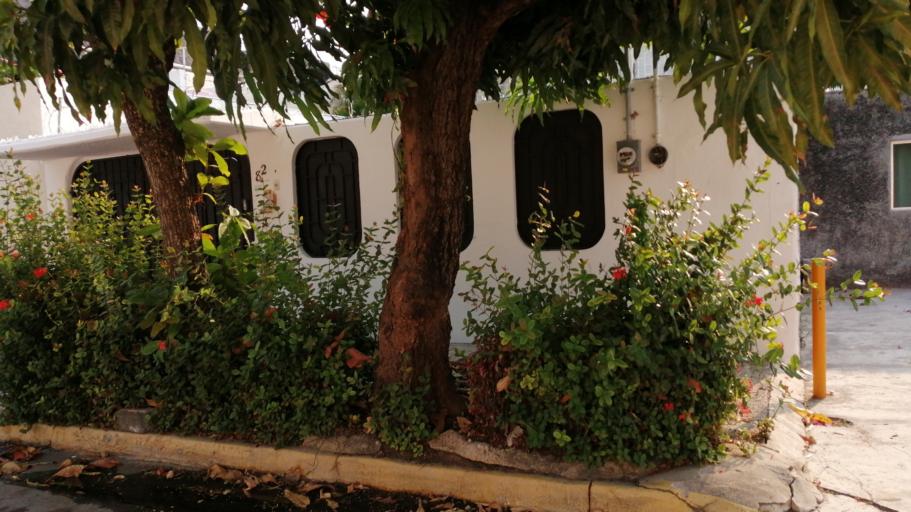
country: MX
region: Guerrero
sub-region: Acapulco de Juarez
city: Colonia Alborada
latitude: 16.8506
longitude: -99.8446
